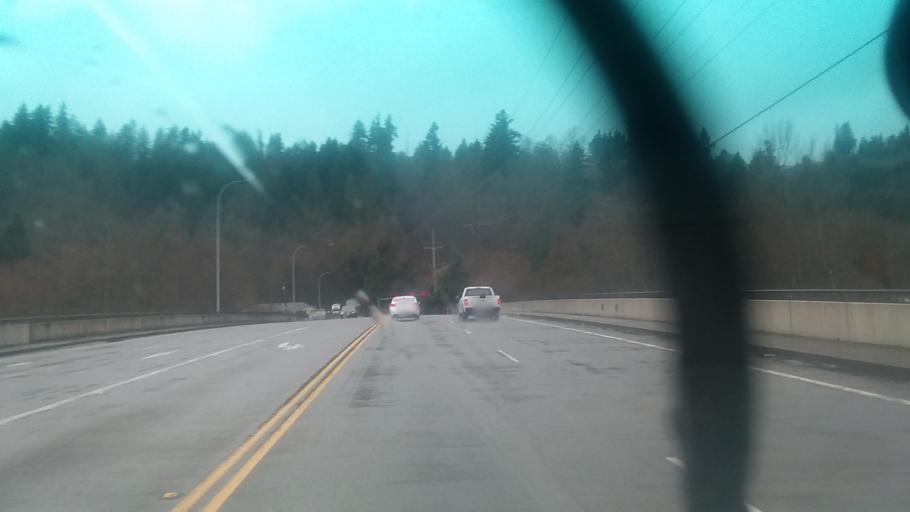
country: US
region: Washington
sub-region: King County
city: Pacific
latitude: 47.2357
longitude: -122.2514
